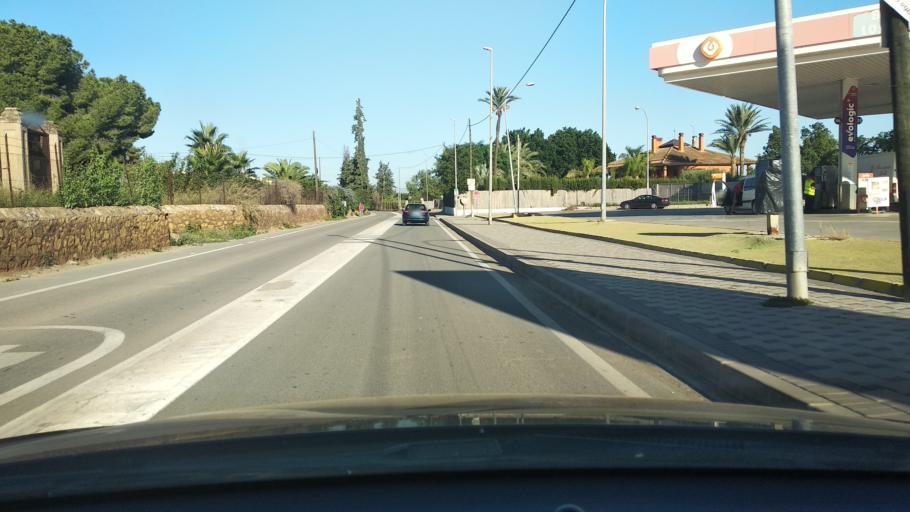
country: ES
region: Murcia
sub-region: Murcia
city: Murcia
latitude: 37.9432
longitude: -1.1187
